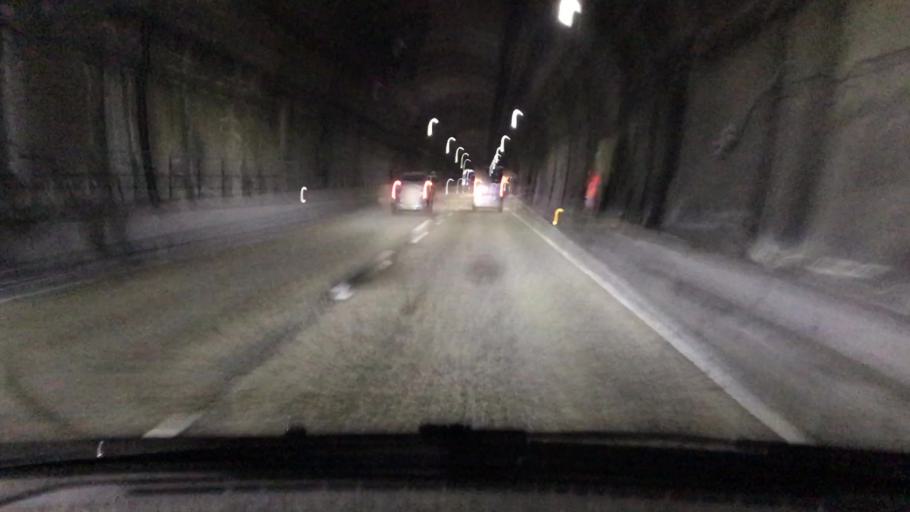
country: JP
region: Hyogo
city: Kobe
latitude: 34.7478
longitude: 135.1678
